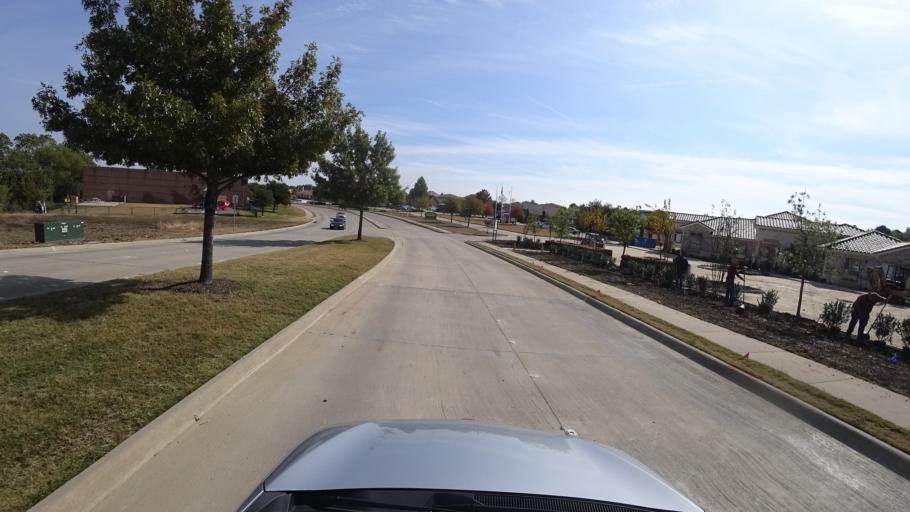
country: US
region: Texas
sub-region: Denton County
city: The Colony
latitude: 33.0359
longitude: -96.8869
